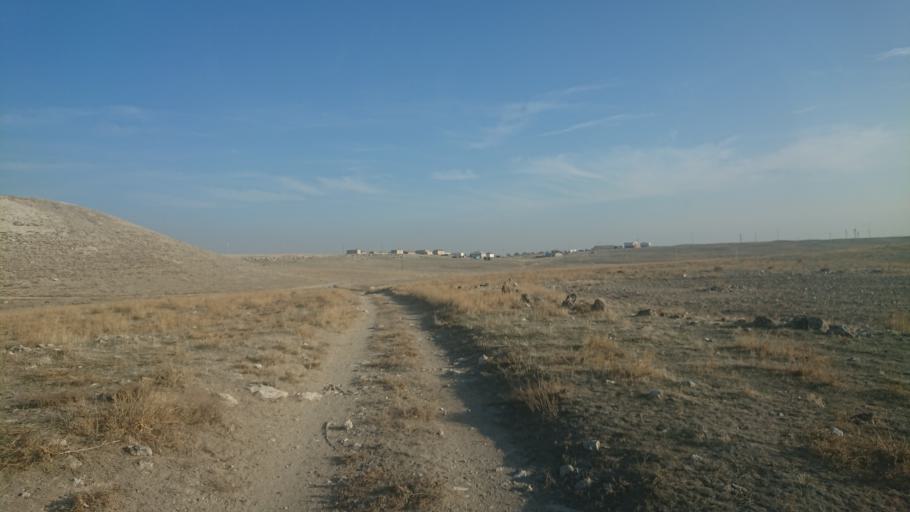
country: TR
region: Aksaray
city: Sultanhani
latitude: 38.1443
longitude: 33.5828
